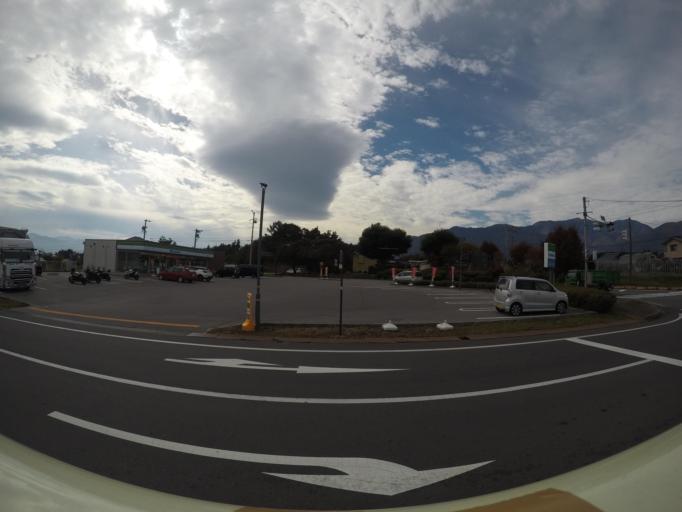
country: JP
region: Nagano
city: Ina
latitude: 35.8555
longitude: 137.9266
